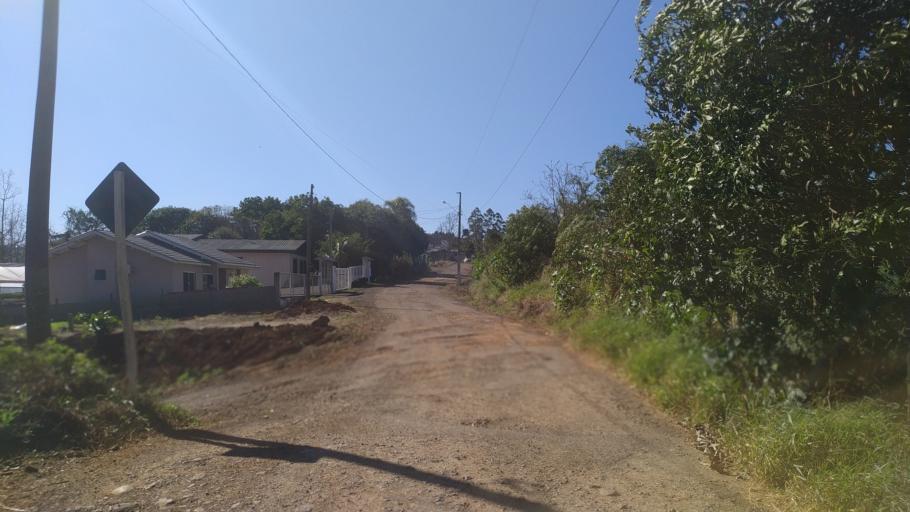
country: BR
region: Santa Catarina
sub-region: Chapeco
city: Chapeco
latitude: -27.1500
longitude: -52.6144
